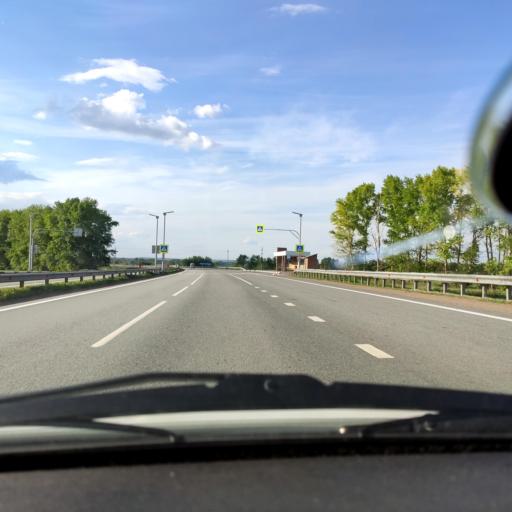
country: RU
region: Bashkortostan
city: Asanovo
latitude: 54.9574
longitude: 55.5843
